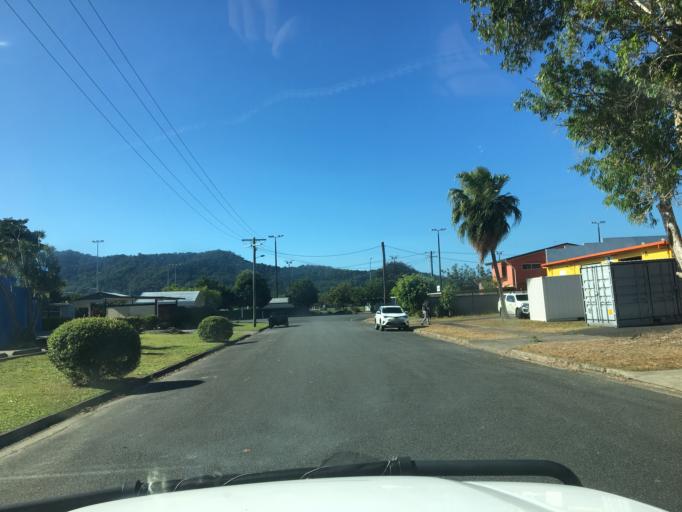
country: AU
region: Queensland
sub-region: Cairns
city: Cairns
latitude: -16.9126
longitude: 145.7464
